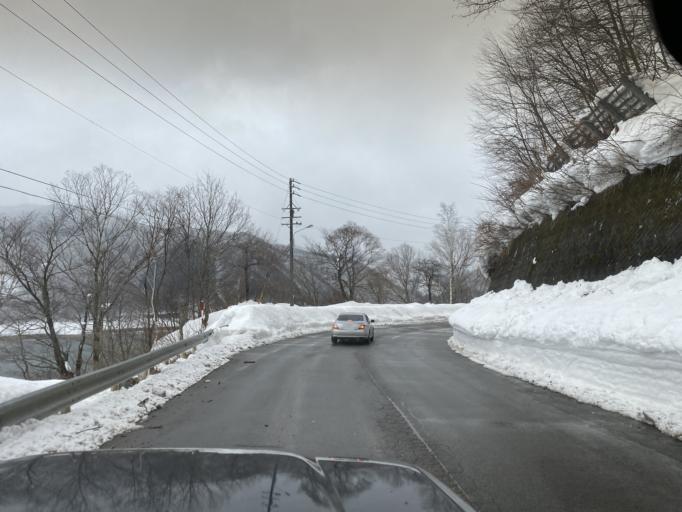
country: JP
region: Gifu
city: Takayama
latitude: 36.1161
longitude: 136.9203
